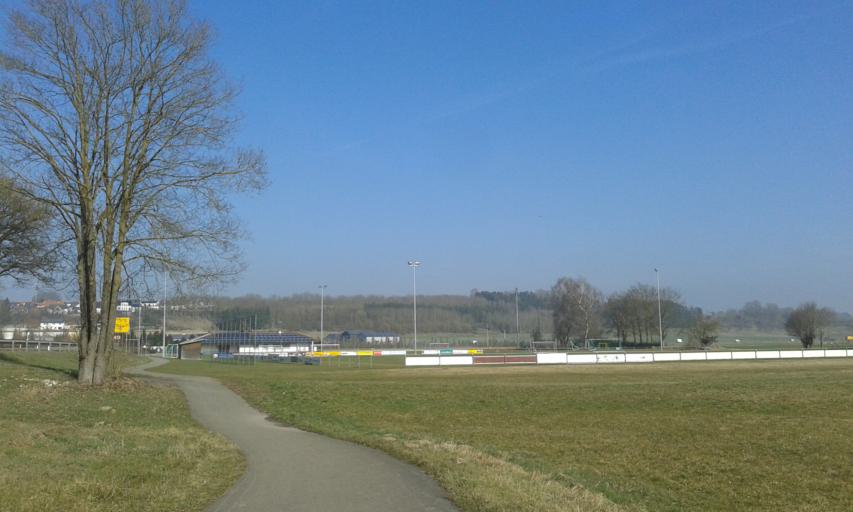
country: DE
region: Baden-Wuerttemberg
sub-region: Tuebingen Region
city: Ersingen
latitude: 48.2983
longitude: 9.8469
